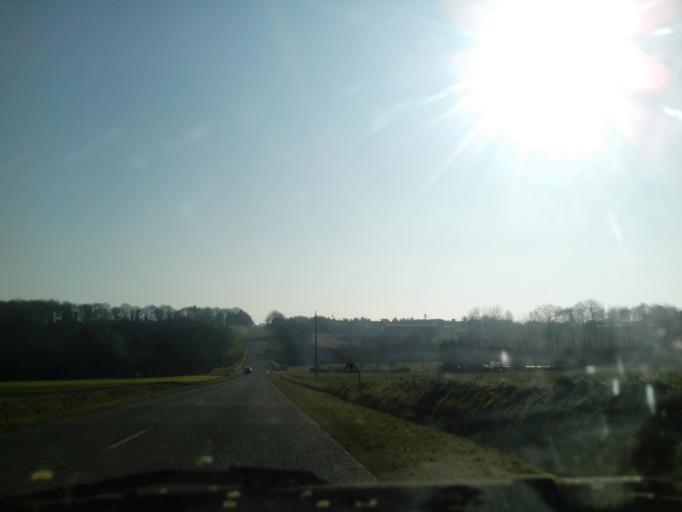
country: FR
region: Brittany
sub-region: Departement du Morbihan
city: Meneac
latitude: 48.1592
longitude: -2.4449
